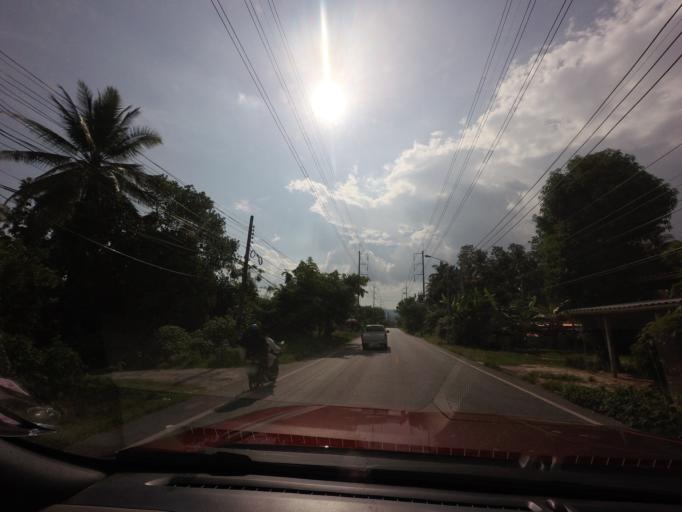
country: TH
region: Yala
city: Yala
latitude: 6.5724
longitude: 101.2023
